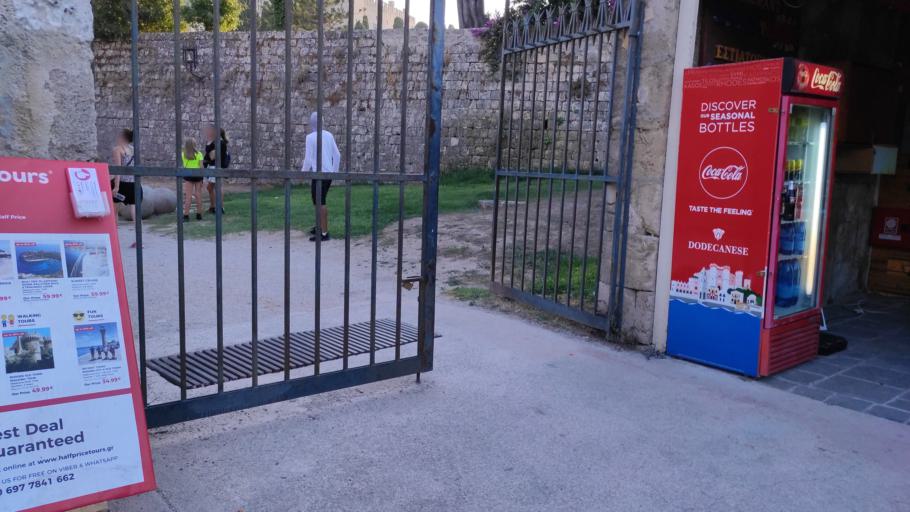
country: GR
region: South Aegean
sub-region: Nomos Dodekanisou
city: Rodos
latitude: 36.4468
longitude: 28.2259
